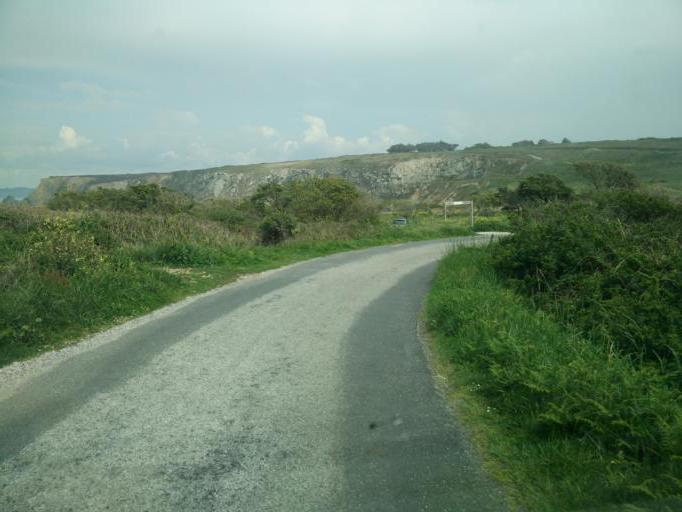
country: FR
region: Brittany
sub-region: Departement du Finistere
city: Camaret-sur-Mer
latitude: 48.2797
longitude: -4.6177
